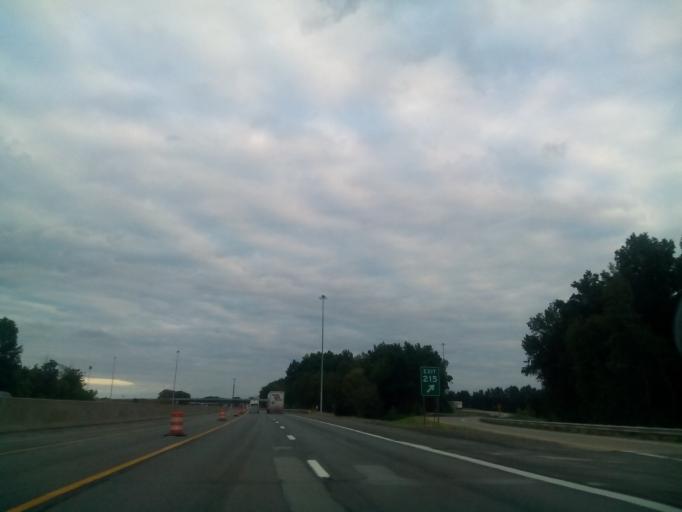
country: US
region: Ohio
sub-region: Trumbull County
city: Lordstown
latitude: 41.1536
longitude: -80.8957
